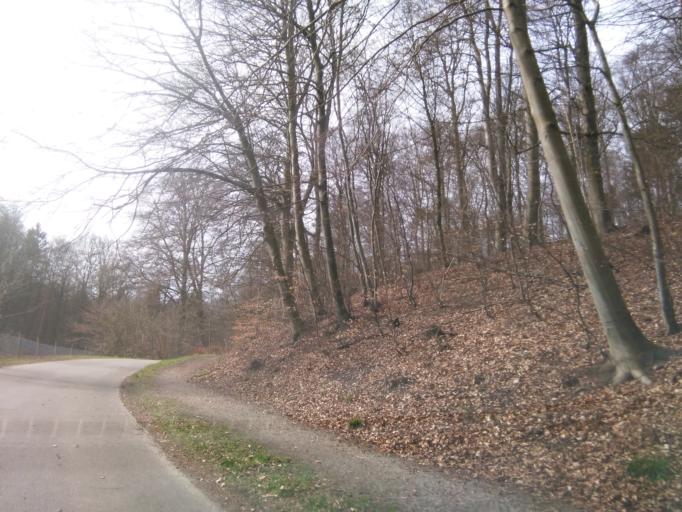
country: DK
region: Central Jutland
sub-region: Arhus Kommune
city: Arhus
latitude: 56.1230
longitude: 10.2158
